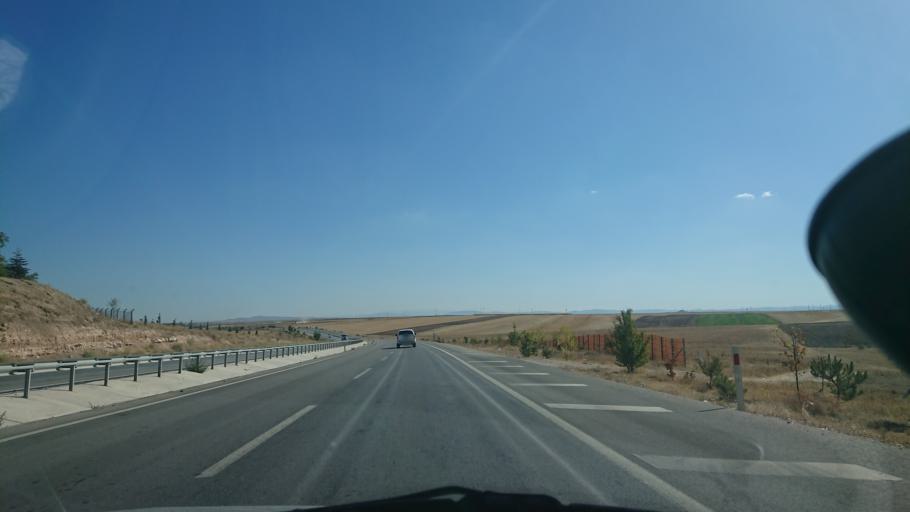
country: TR
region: Eskisehir
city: Mahmudiye
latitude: 39.5044
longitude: 30.9661
